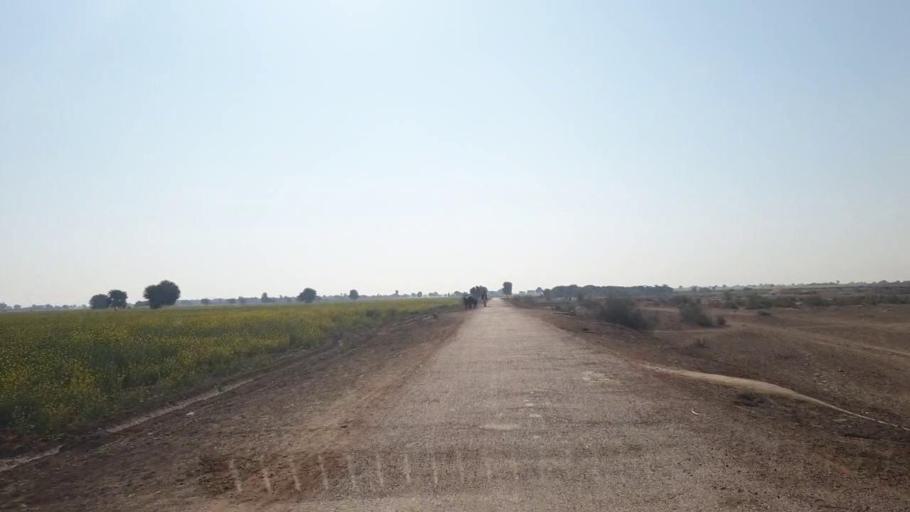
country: PK
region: Sindh
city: Shahpur Chakar
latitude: 26.0880
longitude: 68.6228
